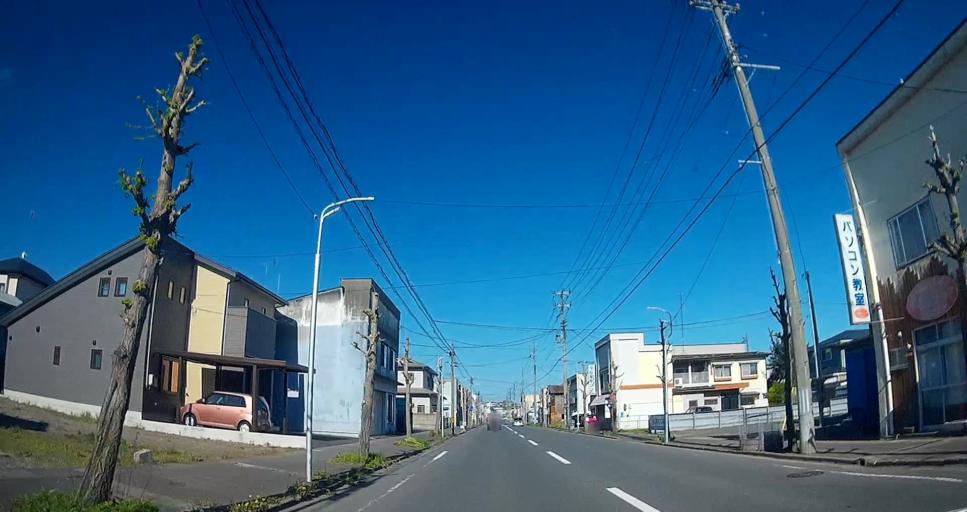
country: JP
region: Aomori
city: Hachinohe
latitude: 40.5224
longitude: 141.5422
